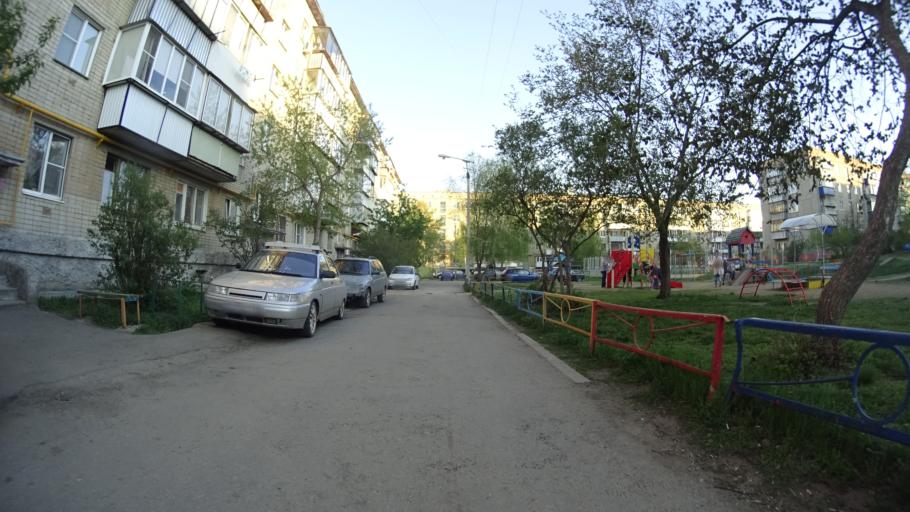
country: RU
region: Chelyabinsk
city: Troitsk
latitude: 54.0819
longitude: 61.5424
